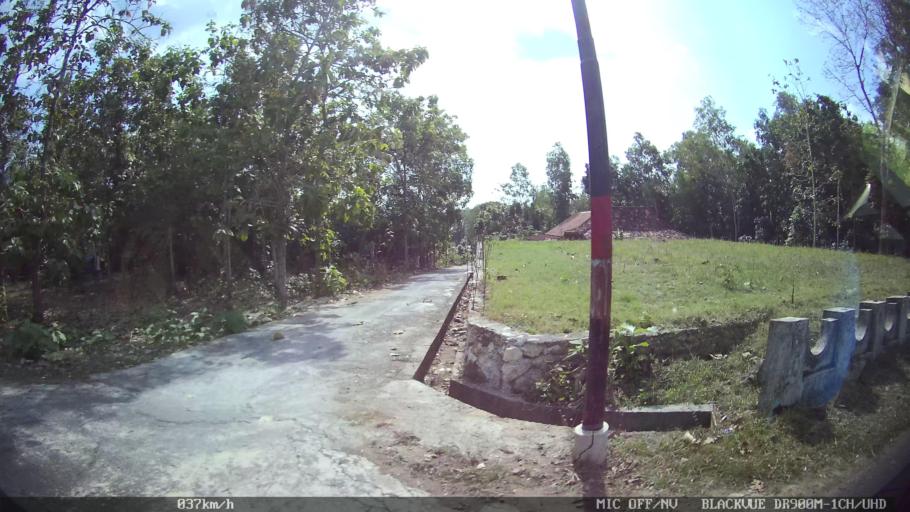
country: ID
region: Daerah Istimewa Yogyakarta
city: Kasihan
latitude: -7.8562
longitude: 110.3011
